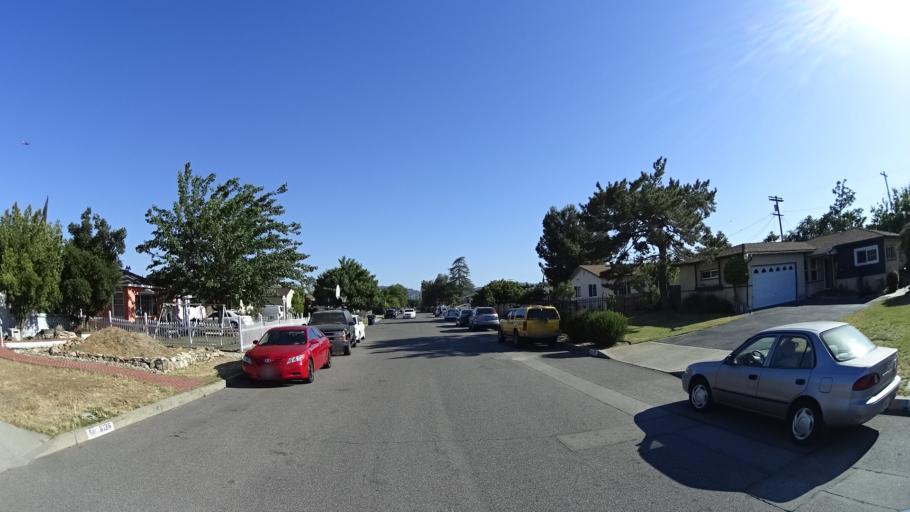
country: US
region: California
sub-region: Los Angeles County
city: North Hollywood
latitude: 34.1823
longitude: -118.3732
